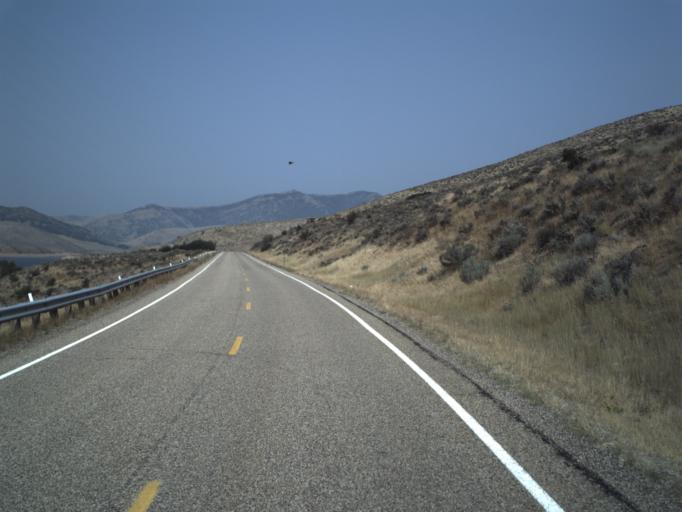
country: US
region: Utah
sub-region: Summit County
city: Summit Park
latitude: 40.8829
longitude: -111.5790
